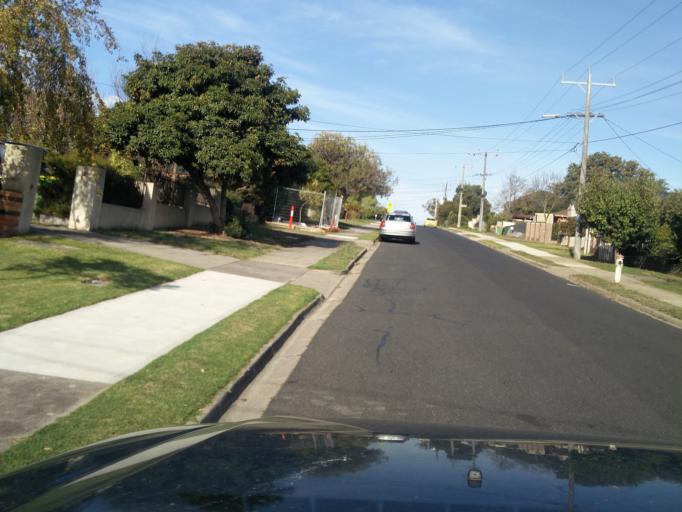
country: AU
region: Victoria
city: Macleod
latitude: -37.7345
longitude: 145.0723
